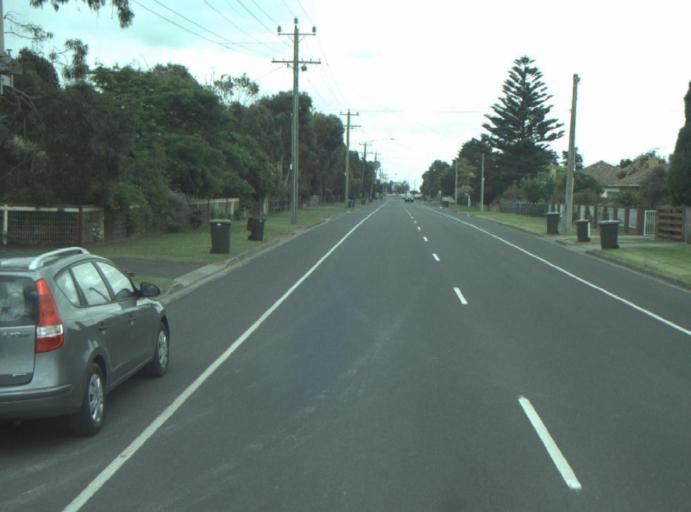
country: AU
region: Victoria
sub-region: Greater Geelong
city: East Geelong
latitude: -38.1672
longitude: 144.4037
